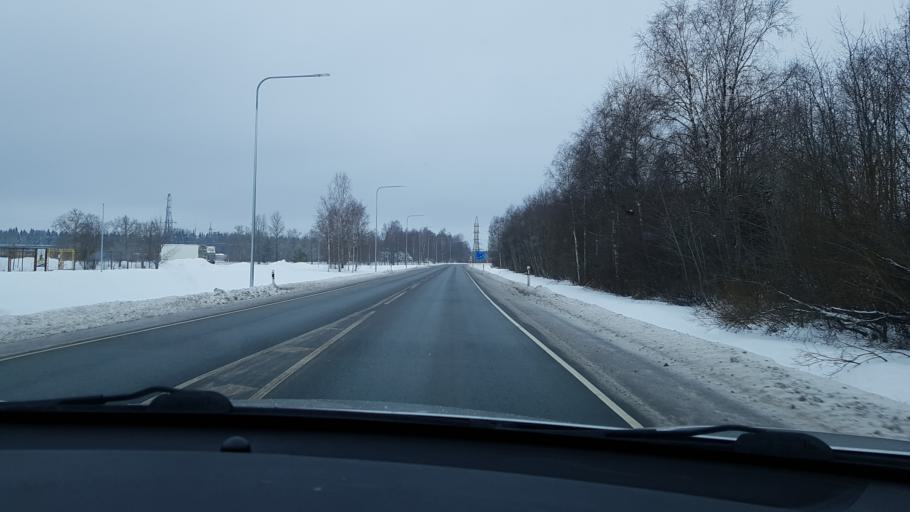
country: EE
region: Jaervamaa
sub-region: Paide linn
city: Paide
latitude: 58.8825
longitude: 25.5319
